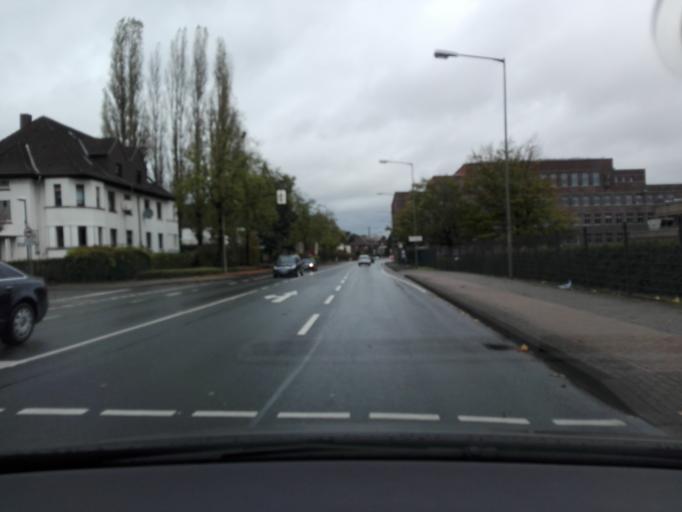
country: DE
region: North Rhine-Westphalia
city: Lunen
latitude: 51.6108
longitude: 7.5097
